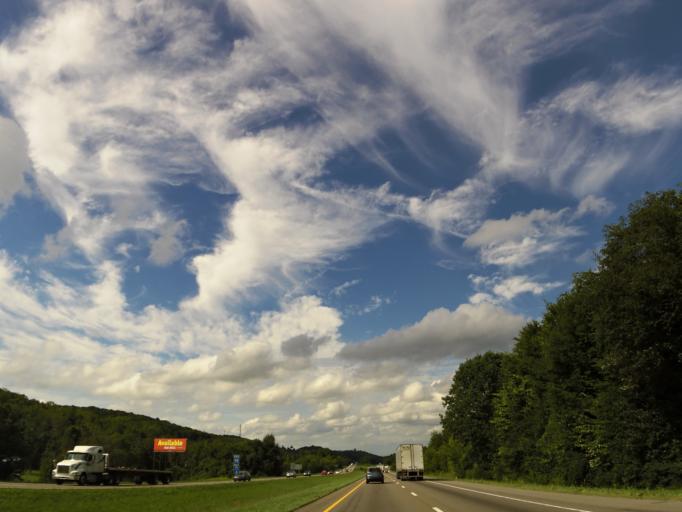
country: US
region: Tennessee
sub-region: Loudon County
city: Lenoir City
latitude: 35.8113
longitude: -84.3023
